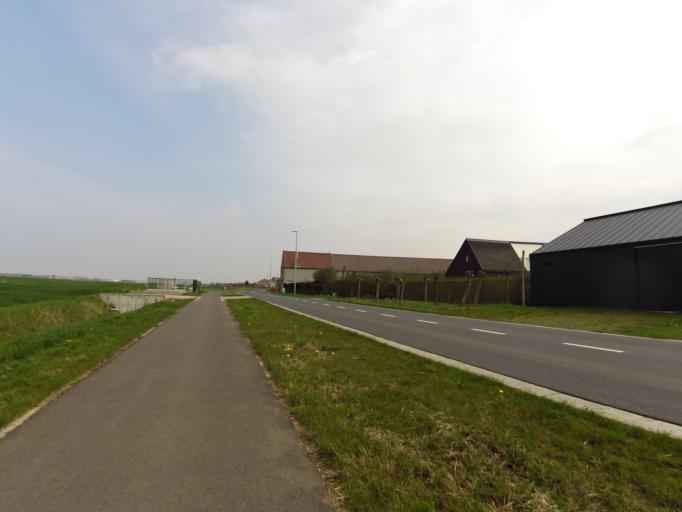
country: BE
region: Flanders
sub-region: Provincie West-Vlaanderen
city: Middelkerke
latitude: 51.1790
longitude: 2.8354
